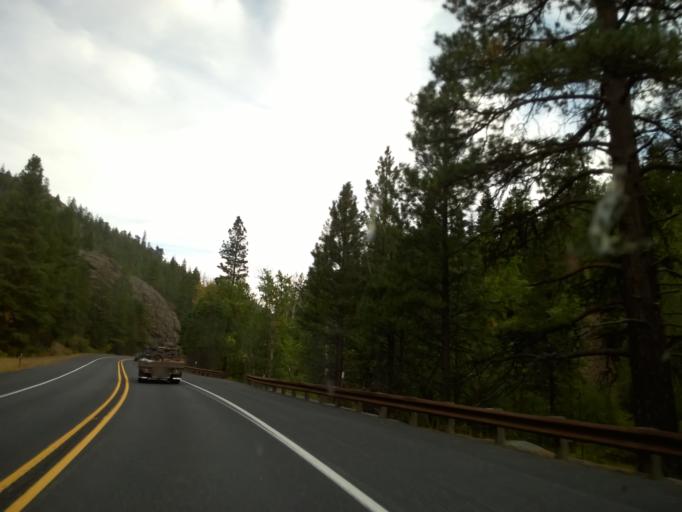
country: US
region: Washington
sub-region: Chelan County
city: Leavenworth
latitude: 47.4121
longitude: -120.6584
